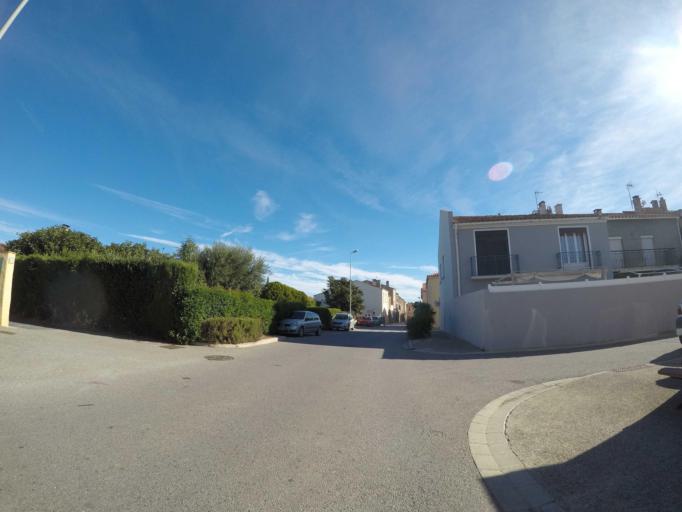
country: FR
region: Languedoc-Roussillon
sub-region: Departement des Pyrenees-Orientales
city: Trouillas
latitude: 42.6094
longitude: 2.8060
